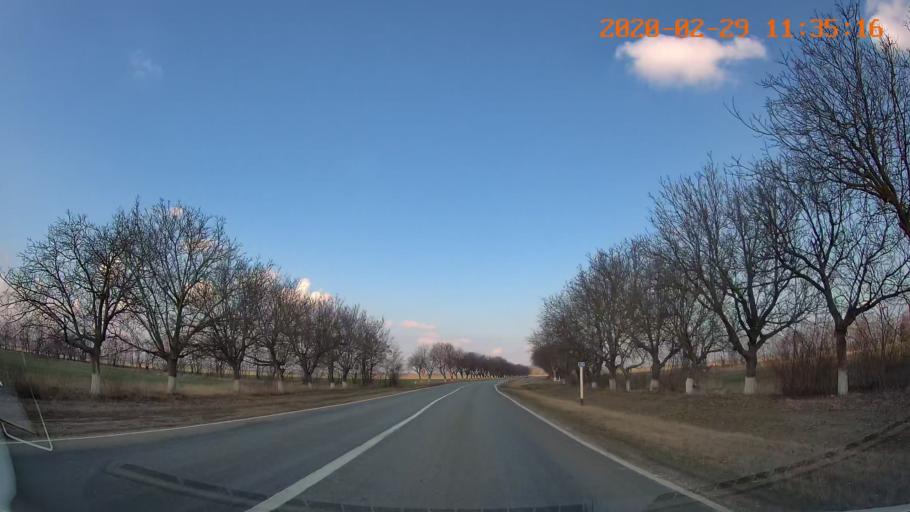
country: MD
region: Rezina
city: Saharna
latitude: 47.5777
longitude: 29.0648
